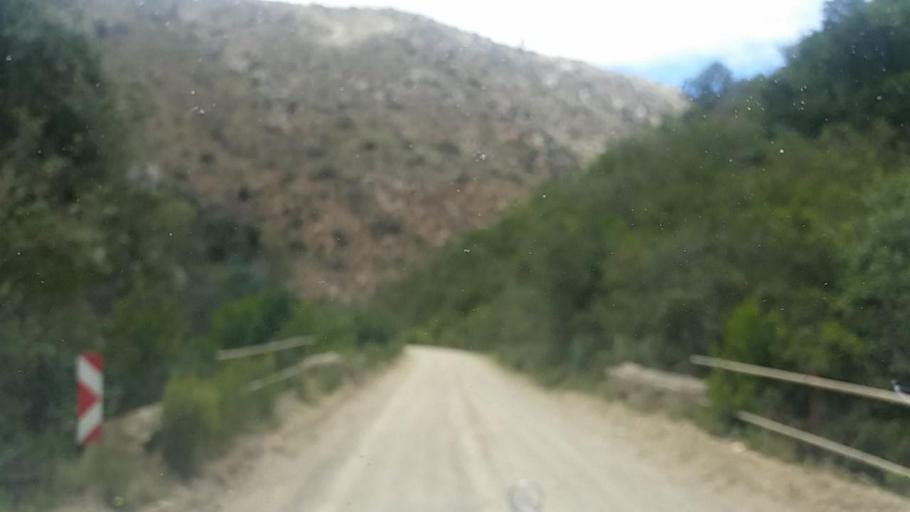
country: ZA
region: Western Cape
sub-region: Eden District Municipality
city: Knysna
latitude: -33.8045
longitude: 23.1811
